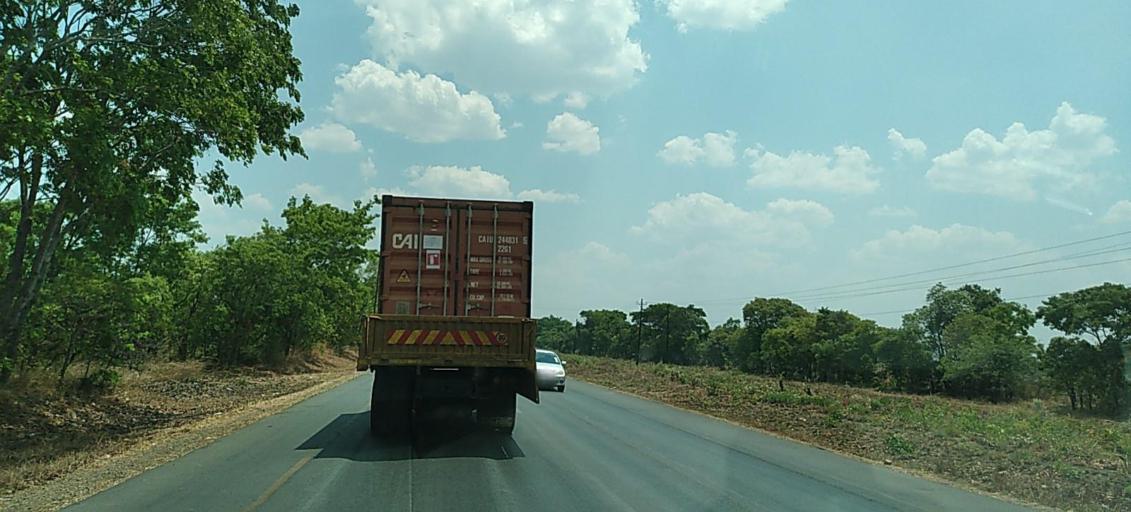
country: ZM
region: Central
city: Kabwe
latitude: -14.3393
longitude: 28.5296
